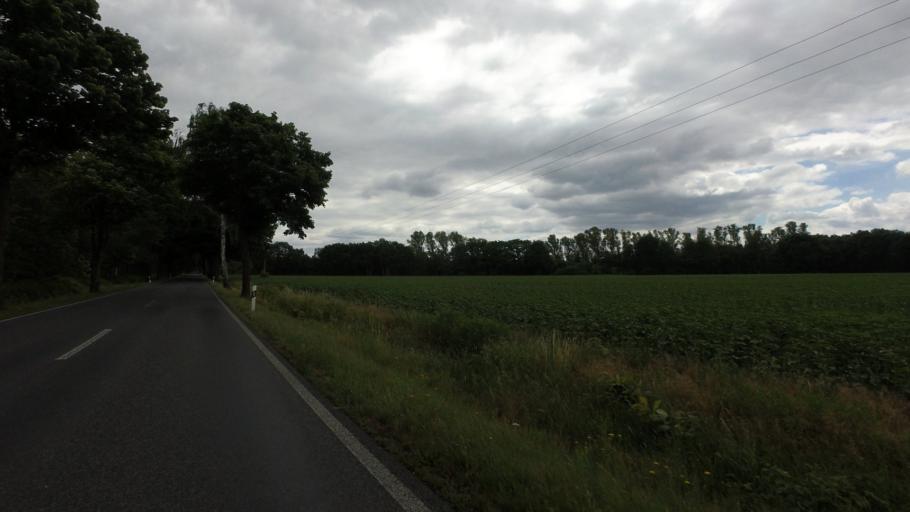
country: DE
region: Brandenburg
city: Calau
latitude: 51.7942
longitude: 13.8618
